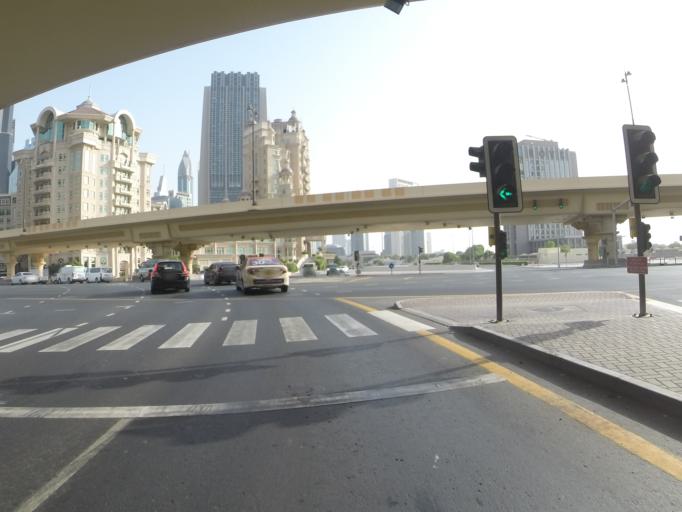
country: AE
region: Dubai
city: Dubai
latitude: 25.2009
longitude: 55.2775
